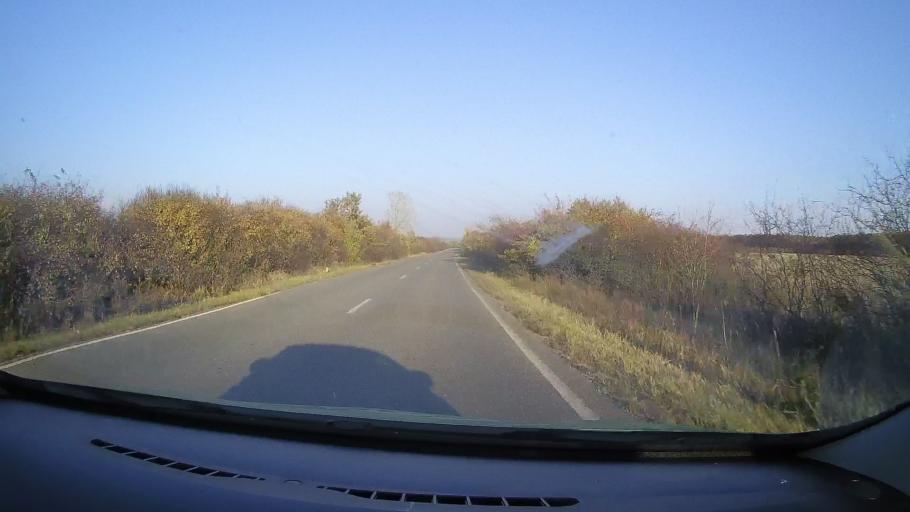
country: RO
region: Arad
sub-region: Comuna Tarnova
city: Chier
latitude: 46.3297
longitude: 21.8451
